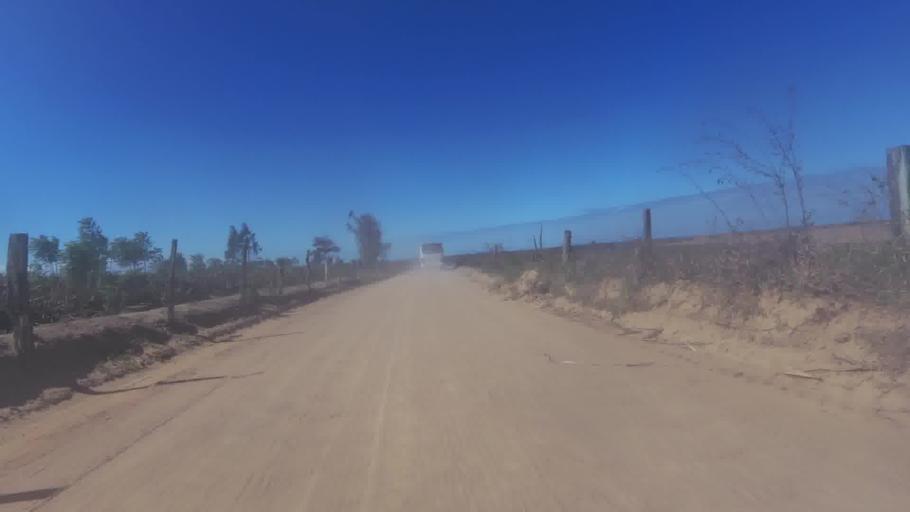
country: BR
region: Espirito Santo
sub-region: Marataizes
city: Marataizes
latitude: -21.1282
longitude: -40.9813
